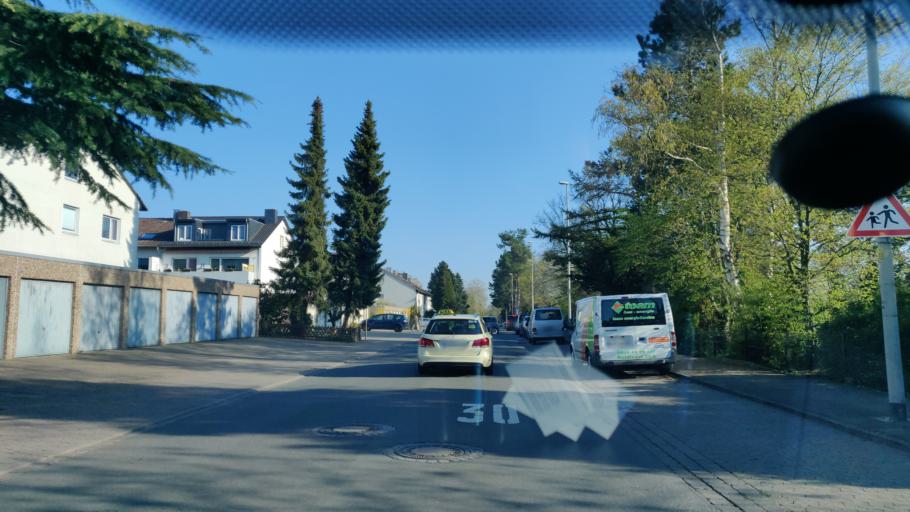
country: DE
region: Lower Saxony
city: Laatzen
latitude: 52.3489
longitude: 9.8341
